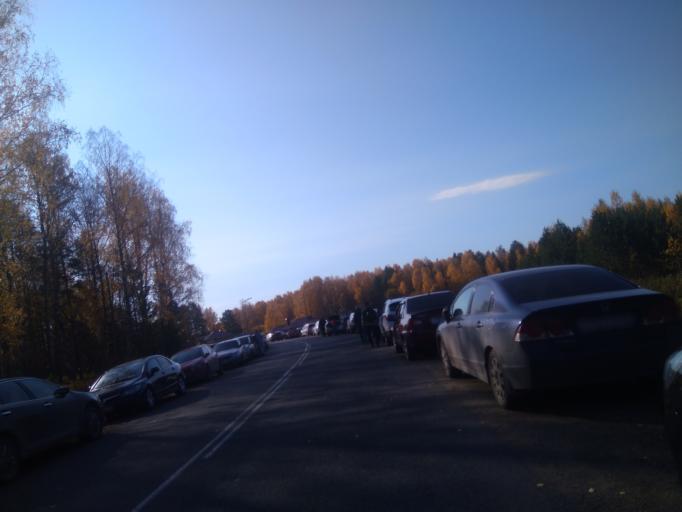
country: RU
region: Sverdlovsk
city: Mikhaylovsk
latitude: 56.5274
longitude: 59.2263
